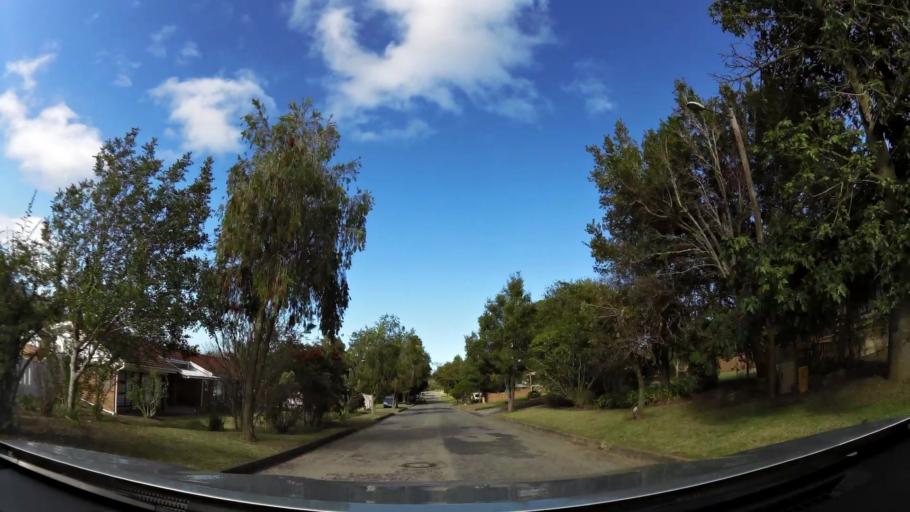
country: ZA
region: Western Cape
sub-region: Eden District Municipality
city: George
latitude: -33.9587
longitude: 22.4945
